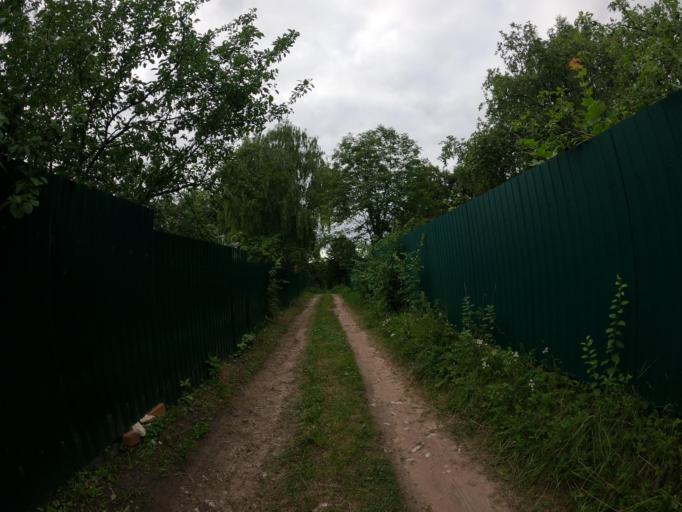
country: RU
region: Moskovskaya
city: Sychevo
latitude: 54.9097
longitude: 38.7323
